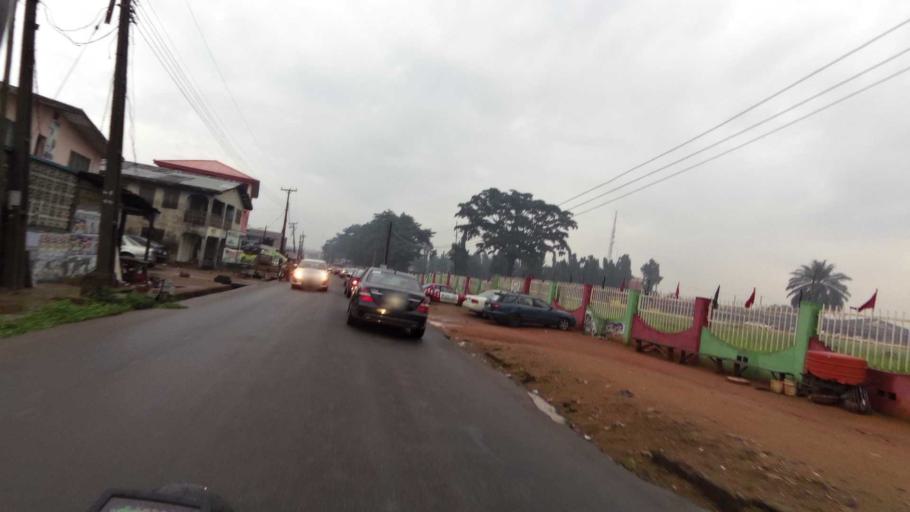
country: NG
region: Oyo
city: Ibadan
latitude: 7.4109
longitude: 3.9303
